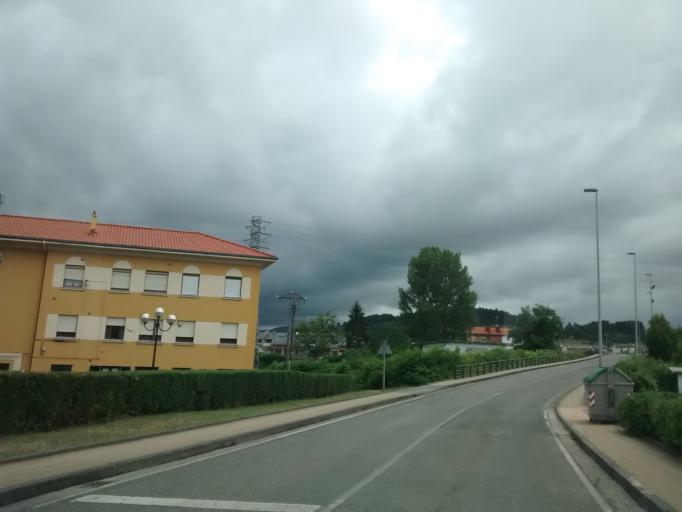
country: ES
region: Cantabria
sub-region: Provincia de Cantabria
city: Torrelavega
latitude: 43.3548
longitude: -4.0598
